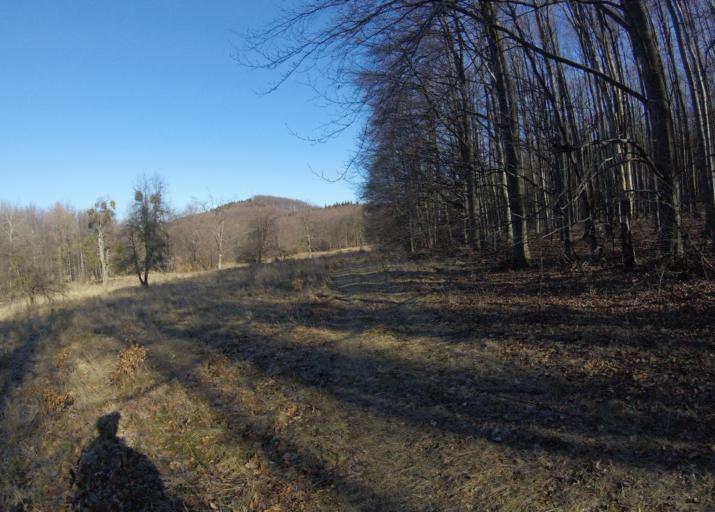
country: HU
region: Heves
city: Szilvasvarad
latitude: 48.0884
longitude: 20.4707
